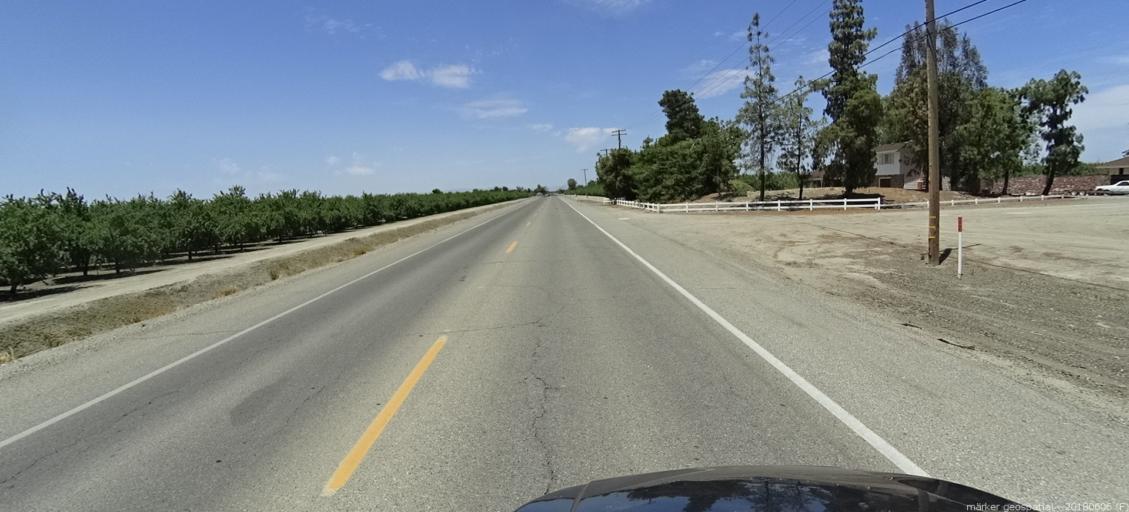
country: US
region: California
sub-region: Fresno County
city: Firebaugh
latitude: 36.8585
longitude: -120.4103
